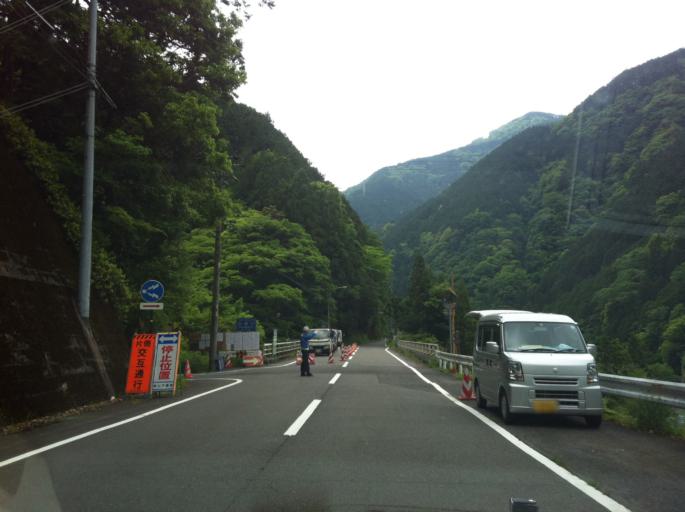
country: JP
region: Shizuoka
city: Shizuoka-shi
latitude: 35.1742
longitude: 138.3128
